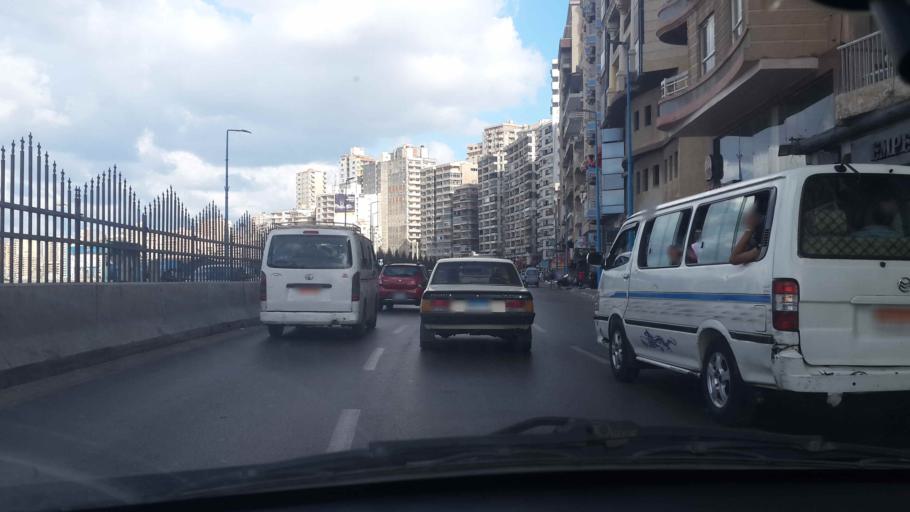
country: EG
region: Alexandria
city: Alexandria
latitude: 31.2701
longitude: 29.9893
